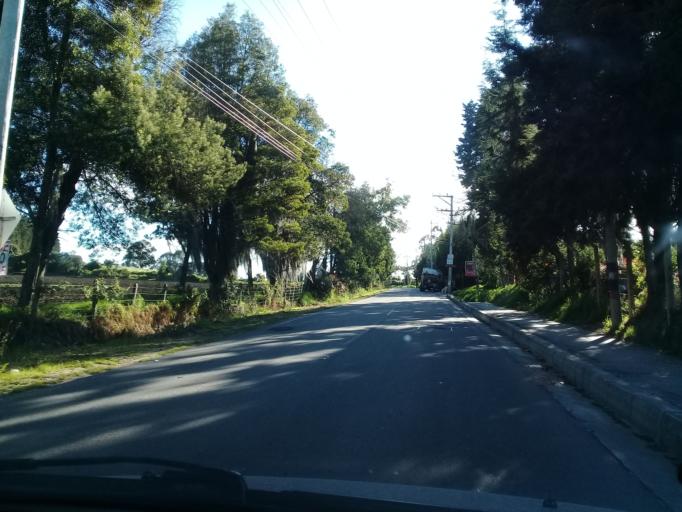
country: CO
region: Cundinamarca
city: Tabio
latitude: 4.9056
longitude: -74.1045
